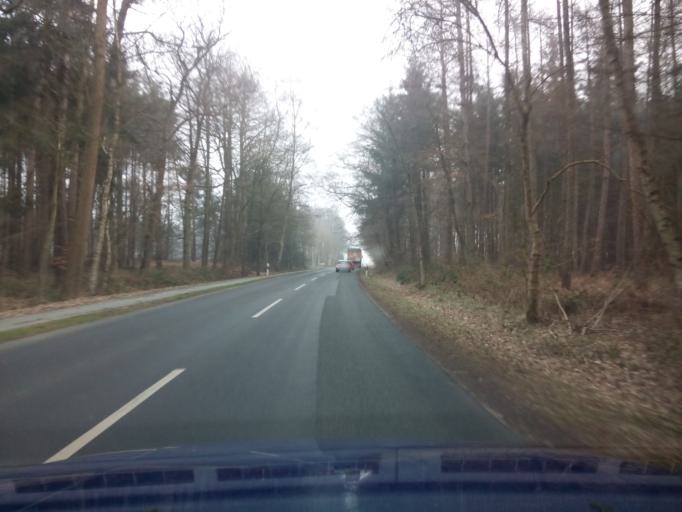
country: DE
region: Lower Saxony
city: Schiffdorf
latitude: 53.6024
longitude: 8.6701
